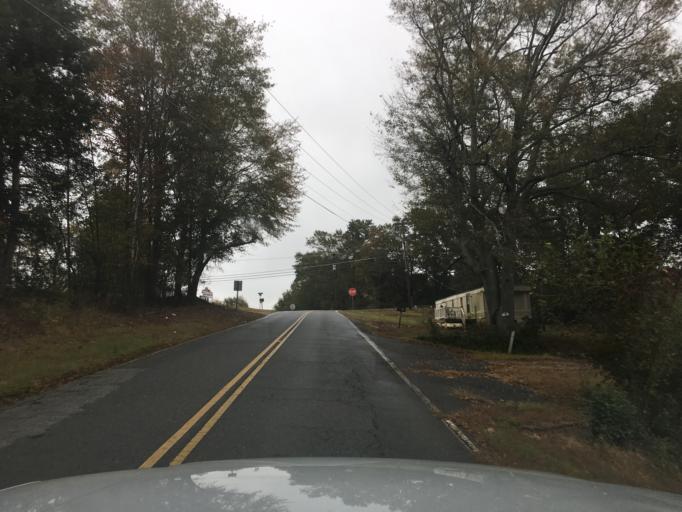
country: US
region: South Carolina
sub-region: Pickens County
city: Central
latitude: 34.7637
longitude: -82.7536
